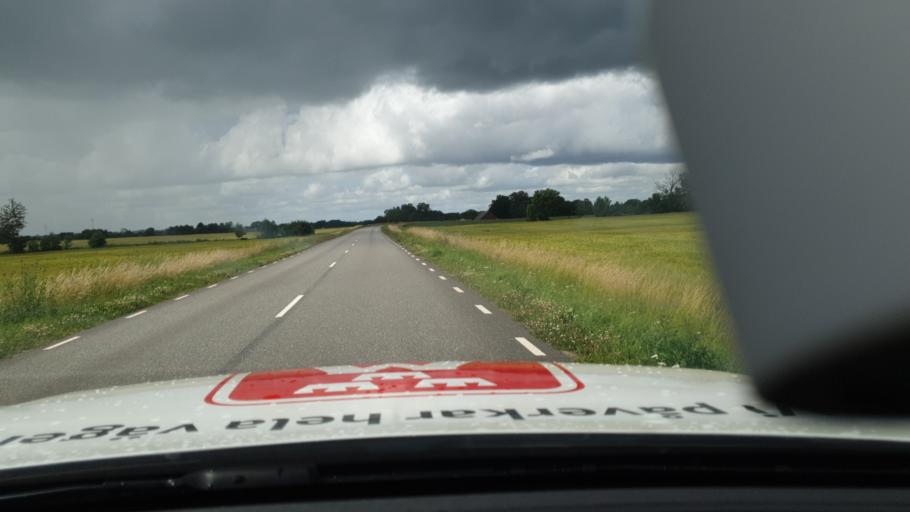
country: SE
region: Vaestra Goetaland
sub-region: Falkopings Kommun
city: Akarp
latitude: 58.2028
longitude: 13.6086
